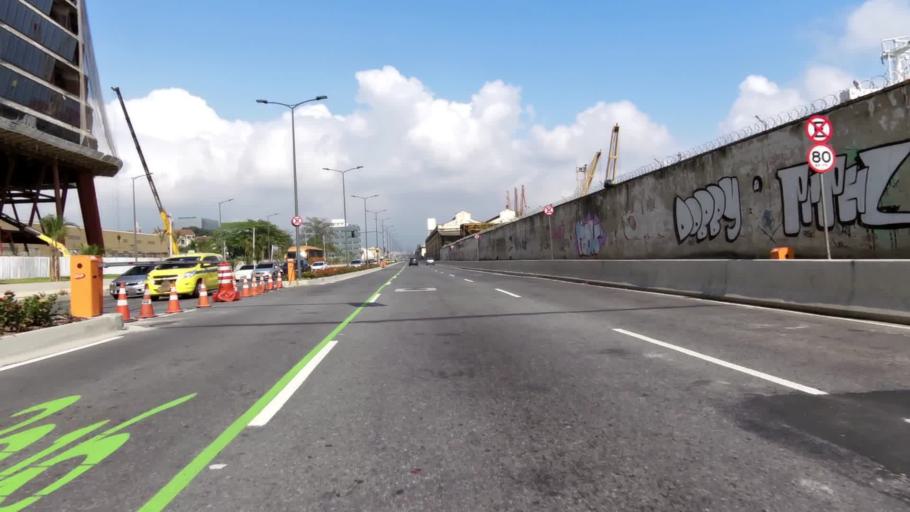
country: BR
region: Rio de Janeiro
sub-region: Rio De Janeiro
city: Rio de Janeiro
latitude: -22.8931
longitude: -43.1968
